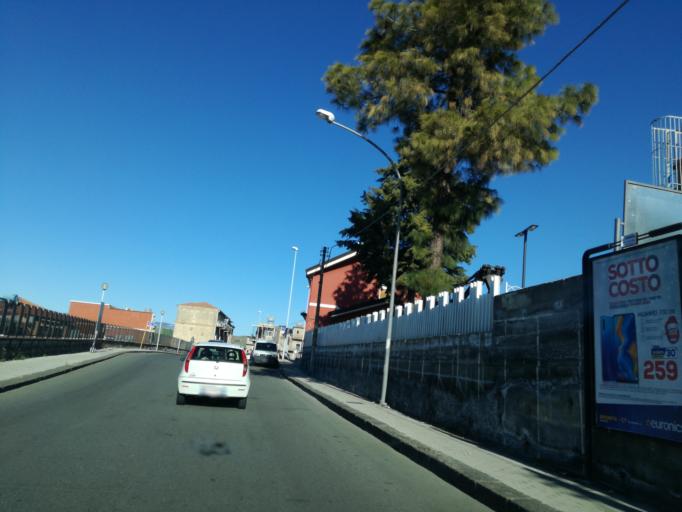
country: IT
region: Sicily
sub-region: Catania
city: Bronte
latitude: 37.7874
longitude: 14.8382
